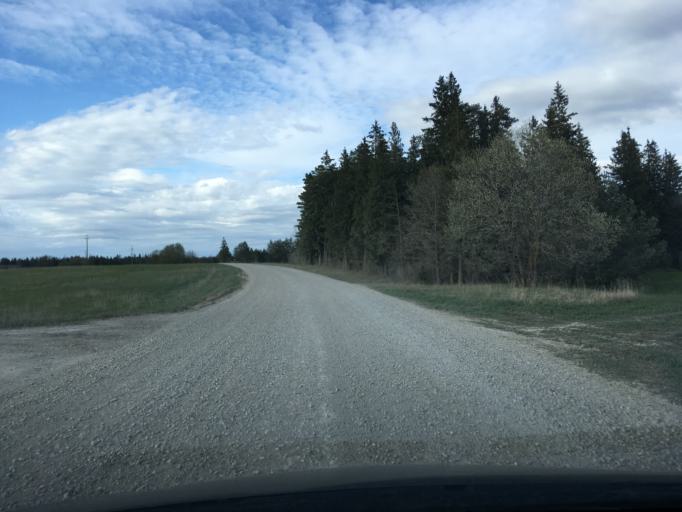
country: EE
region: Raplamaa
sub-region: Maerjamaa vald
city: Marjamaa
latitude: 58.9450
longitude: 24.3178
